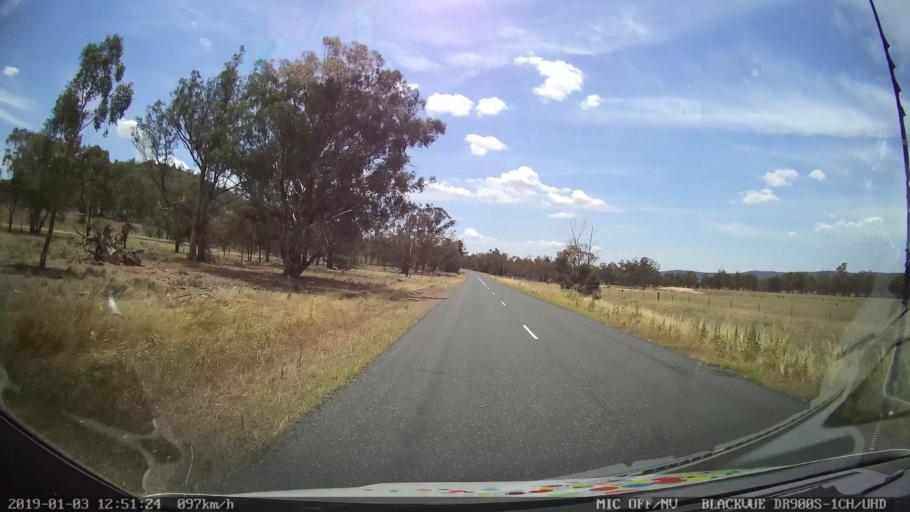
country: AU
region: New South Wales
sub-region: Weddin
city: Grenfell
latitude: -33.6802
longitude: 148.2800
